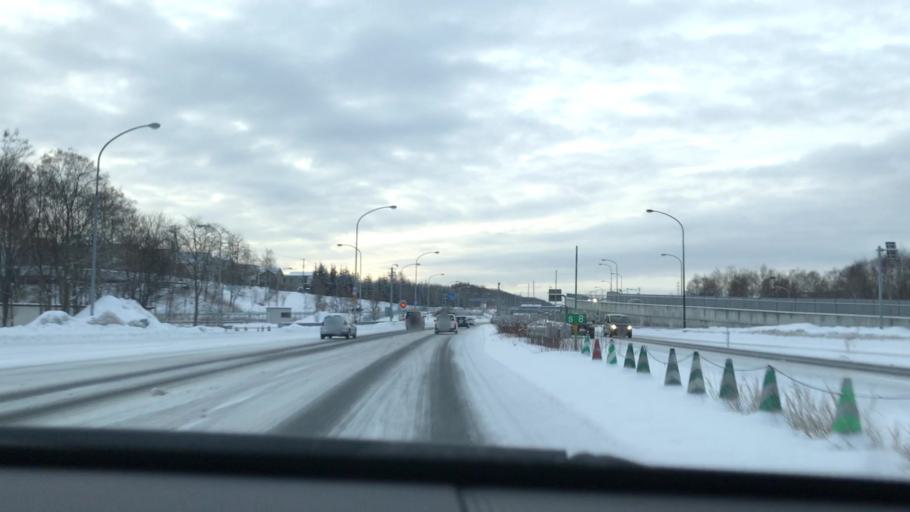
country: JP
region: Hokkaido
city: Kitahiroshima
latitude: 43.0145
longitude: 141.4645
